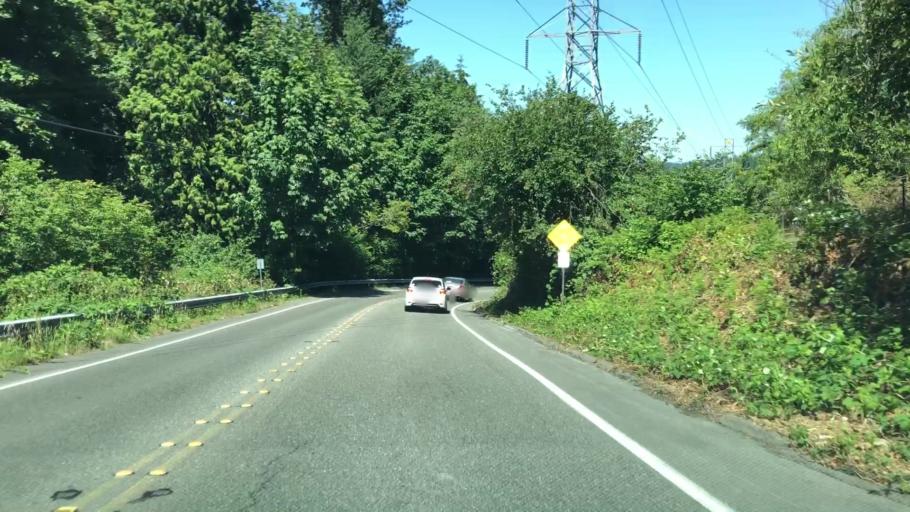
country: US
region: Washington
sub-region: King County
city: Woodinville
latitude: 47.7528
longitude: -122.1746
